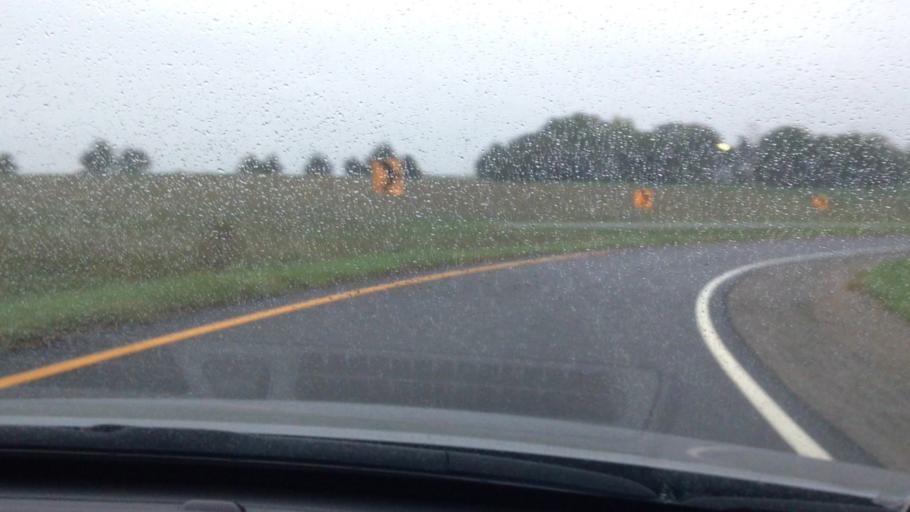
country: US
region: Kansas
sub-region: Brown County
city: Hiawatha
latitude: 39.8401
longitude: -95.5472
